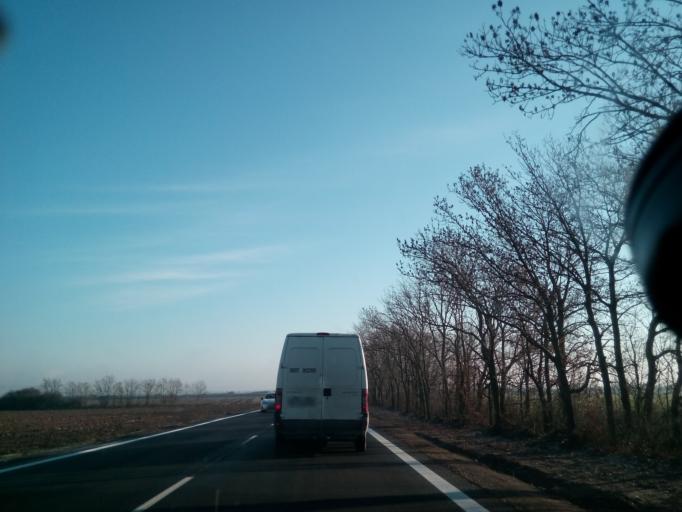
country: SK
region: Kosicky
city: Trebisov
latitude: 48.7003
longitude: 21.7380
